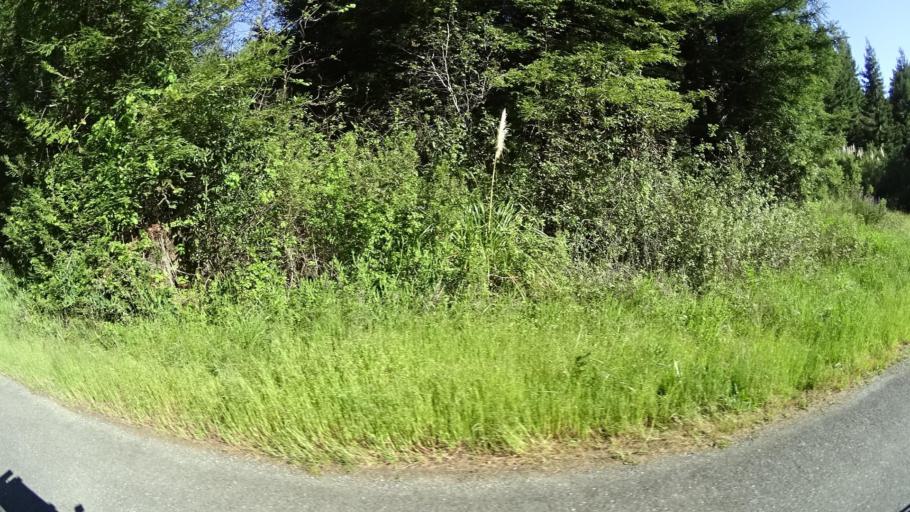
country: US
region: California
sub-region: Humboldt County
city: Rio Dell
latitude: 40.4343
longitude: -123.9662
